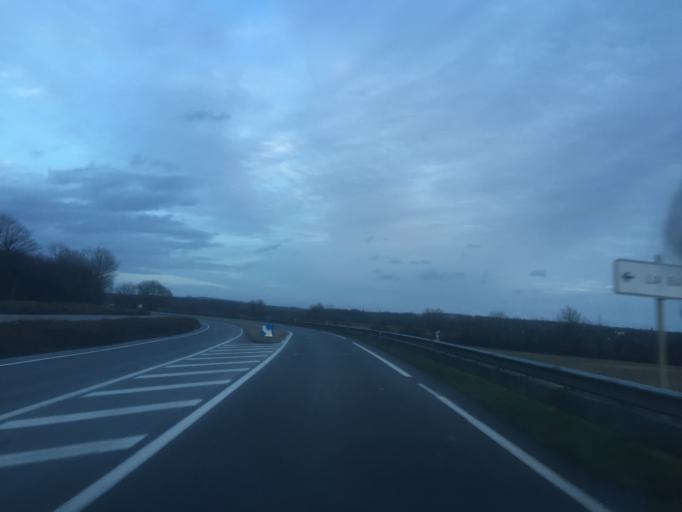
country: FR
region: Franche-Comte
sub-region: Departement du Jura
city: Orchamps
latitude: 47.1427
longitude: 5.6766
